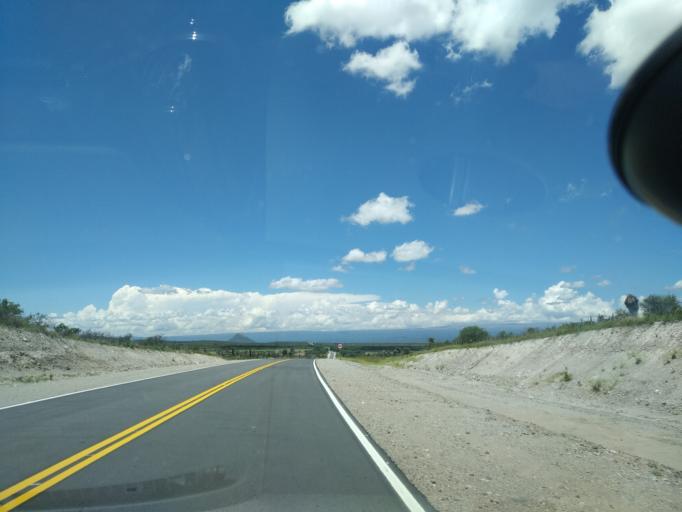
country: AR
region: Cordoba
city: Salsacate
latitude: -31.3738
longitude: -65.2745
